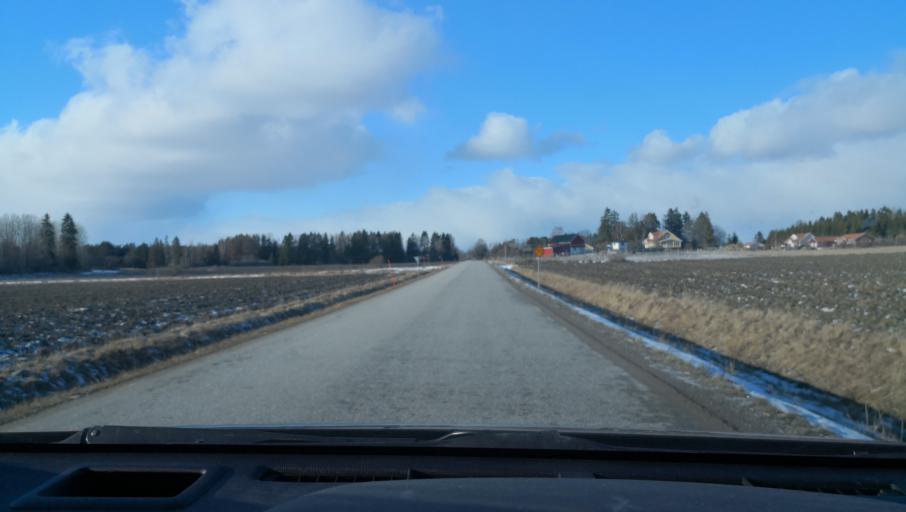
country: SE
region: Uppsala
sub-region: Enkopings Kommun
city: Hummelsta
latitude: 59.6312
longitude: 16.9767
